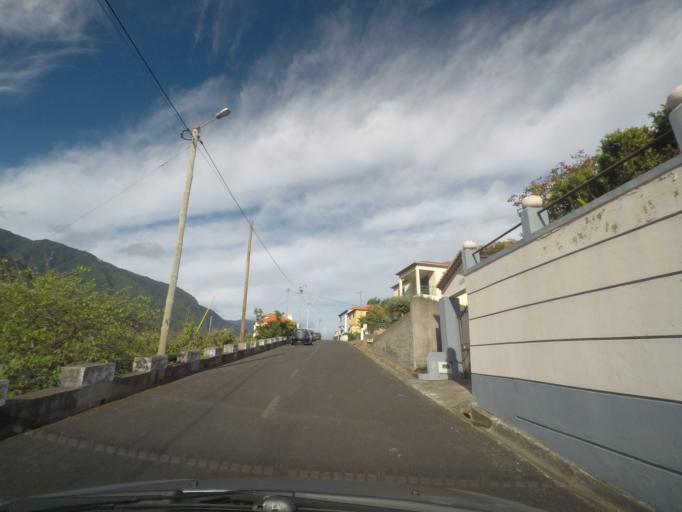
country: PT
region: Madeira
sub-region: Sao Vicente
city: Sao Vicente
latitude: 32.8270
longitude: -16.9889
